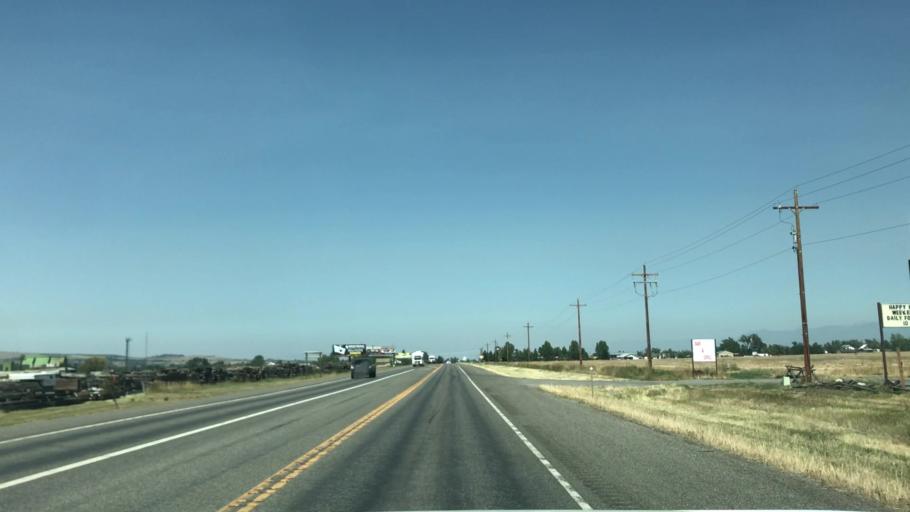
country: US
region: Montana
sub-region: Gallatin County
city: Four Corners
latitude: 45.5840
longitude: -111.1970
